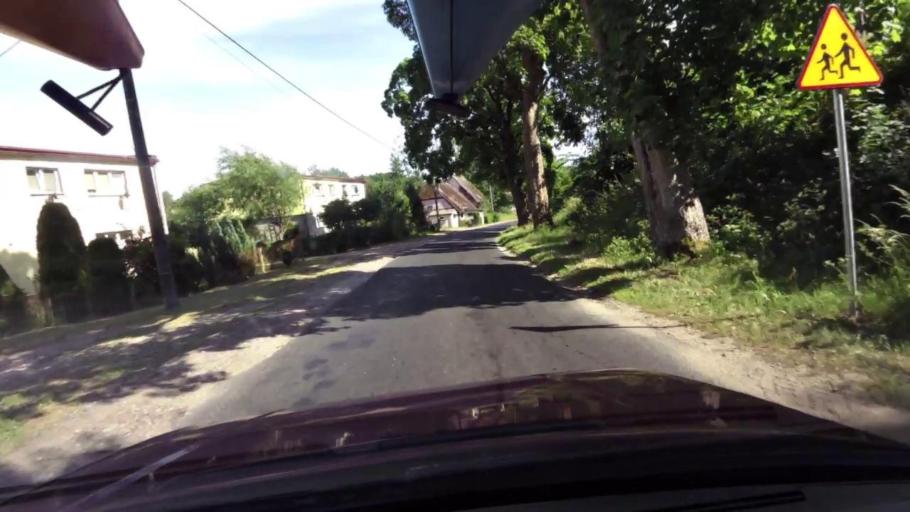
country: PL
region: Pomeranian Voivodeship
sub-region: Powiat bytowski
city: Miastko
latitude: 54.1220
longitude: 16.9444
